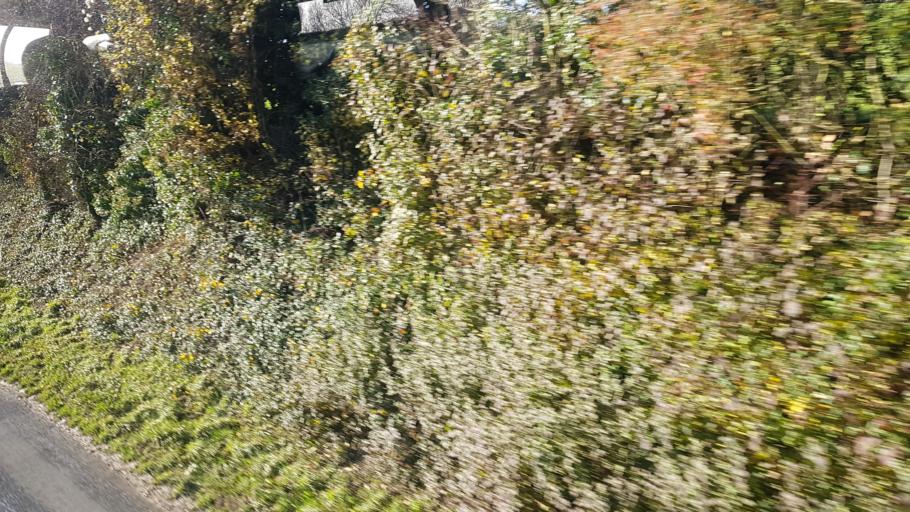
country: GB
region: England
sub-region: Isle of Wight
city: Newport
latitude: 50.6666
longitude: -1.3443
